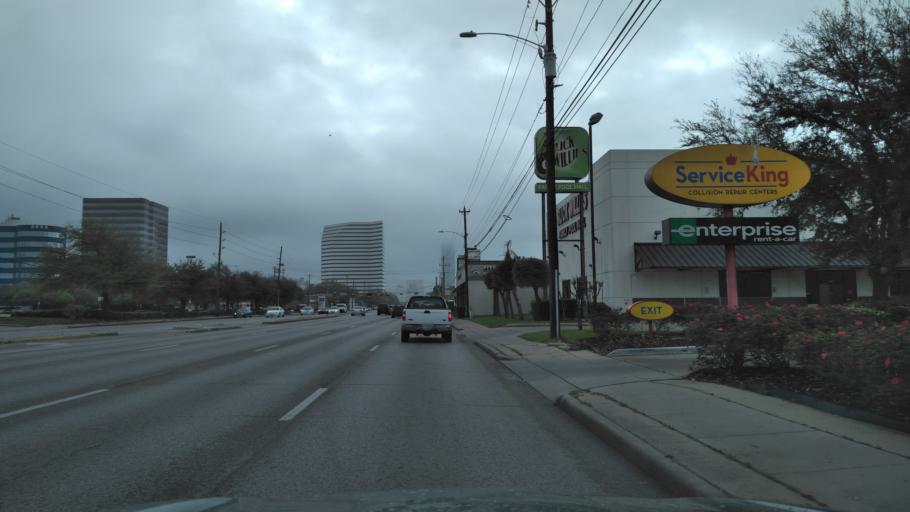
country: US
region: Texas
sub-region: Harris County
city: Hunters Creek Village
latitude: 29.7377
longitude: -95.4864
